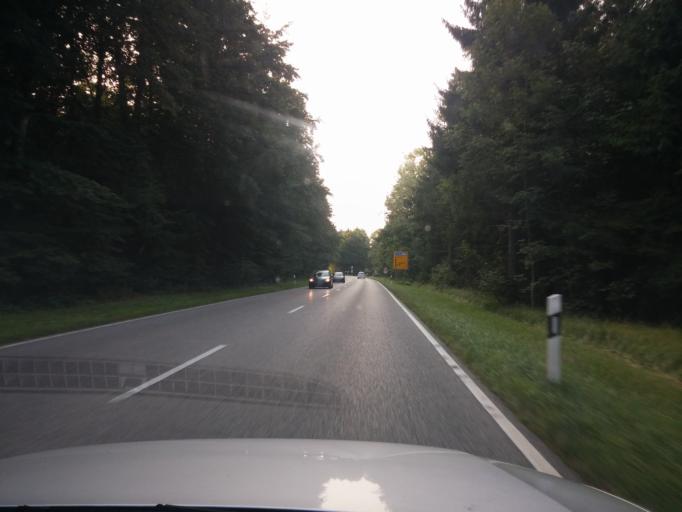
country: DE
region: Bavaria
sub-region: Upper Bavaria
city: Grasbrunn
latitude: 48.0606
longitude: 11.7510
